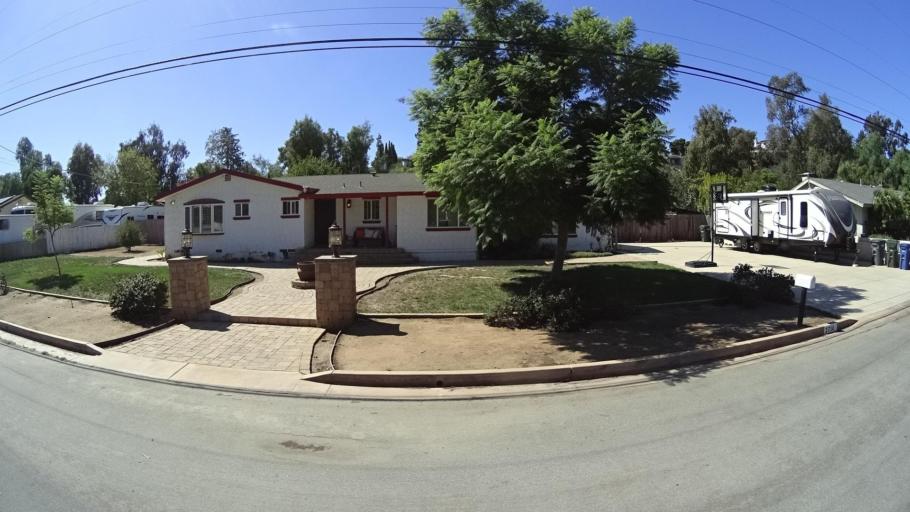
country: US
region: California
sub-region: San Diego County
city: Bonita
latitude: 32.6578
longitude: -117.0505
